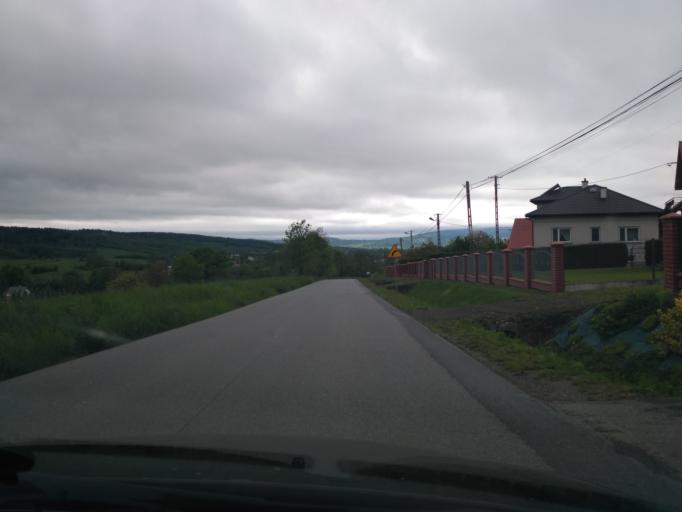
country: PL
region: Subcarpathian Voivodeship
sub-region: Powiat jasielski
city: Kolaczyce
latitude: 49.8030
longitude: 21.4941
